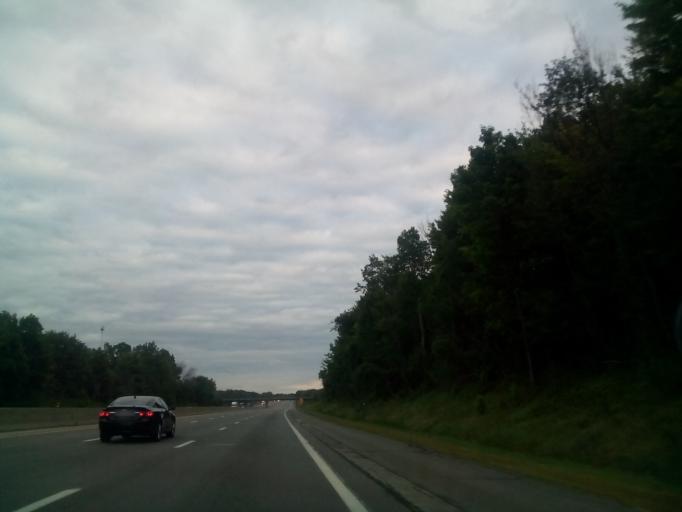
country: US
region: Ohio
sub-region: Portage County
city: Hiram
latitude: 41.2432
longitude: -81.1534
